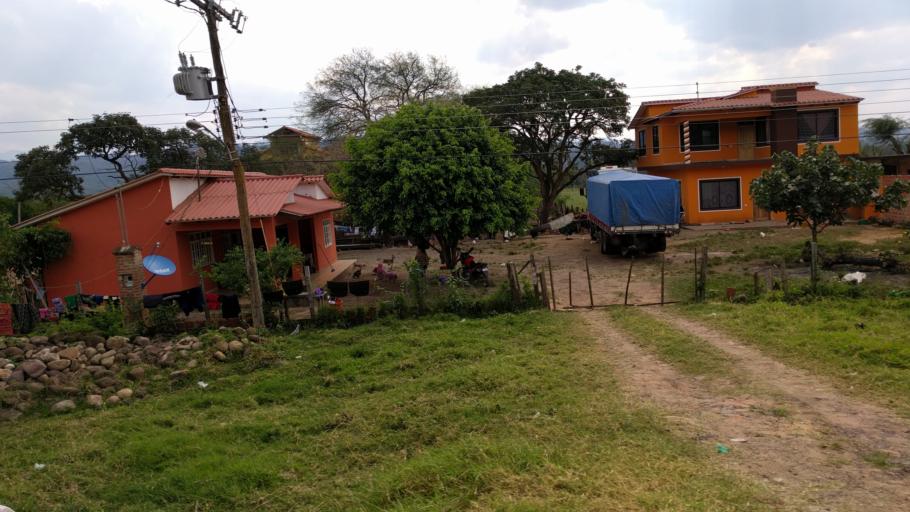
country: BO
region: Santa Cruz
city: Jorochito
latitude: -18.0728
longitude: -63.4426
